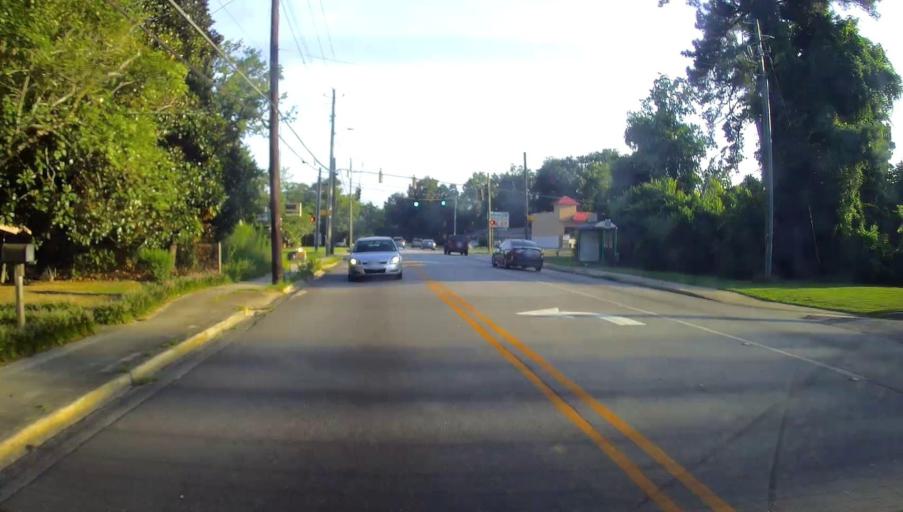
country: US
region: Georgia
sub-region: Bibb County
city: Macon
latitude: 32.8474
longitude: -83.6880
